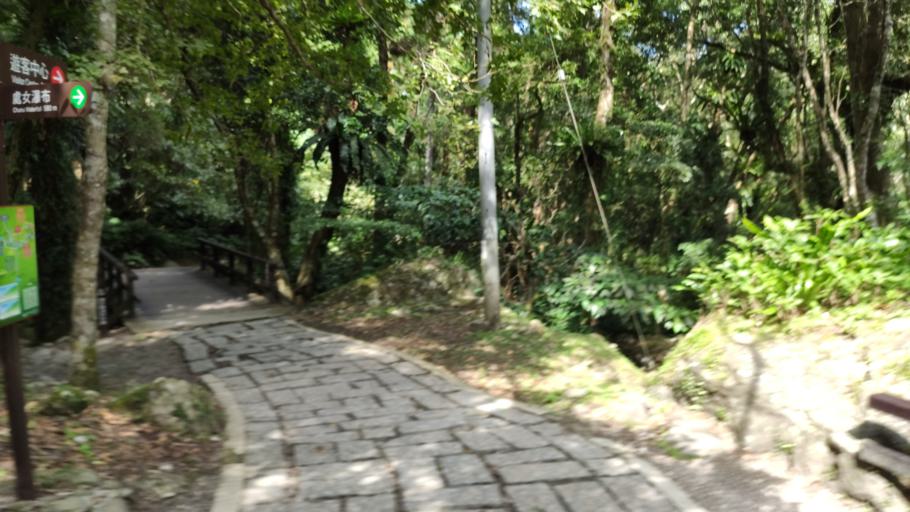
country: TW
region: Taiwan
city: Daxi
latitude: 24.8201
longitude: 121.4500
